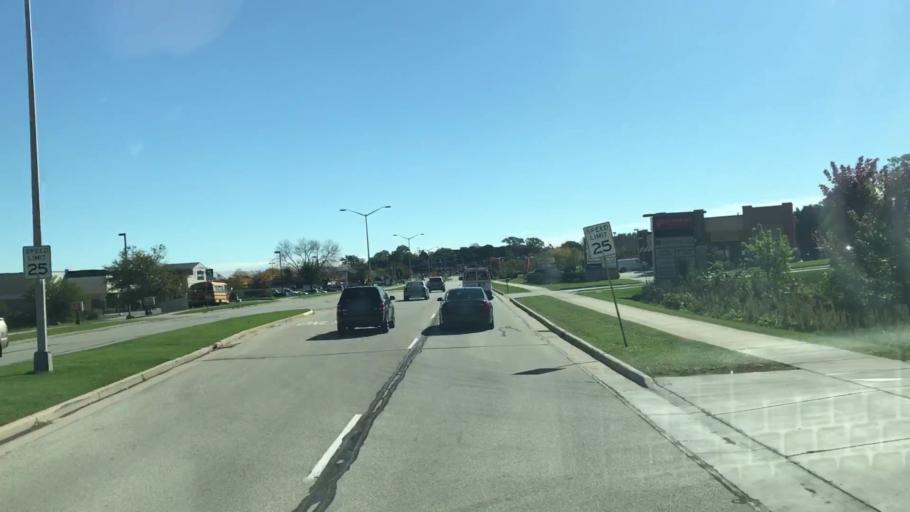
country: US
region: Wisconsin
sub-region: Waukesha County
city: Pewaukee
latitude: 43.0443
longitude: -88.2632
